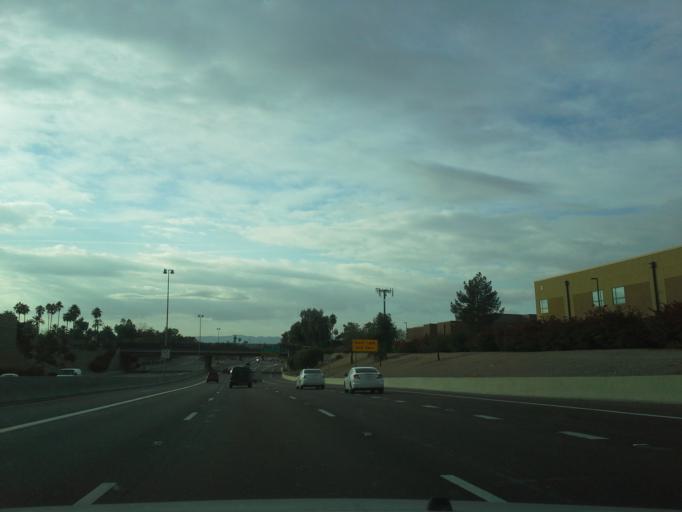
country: US
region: Arizona
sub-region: Maricopa County
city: Phoenix
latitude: 33.5189
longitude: -112.0443
